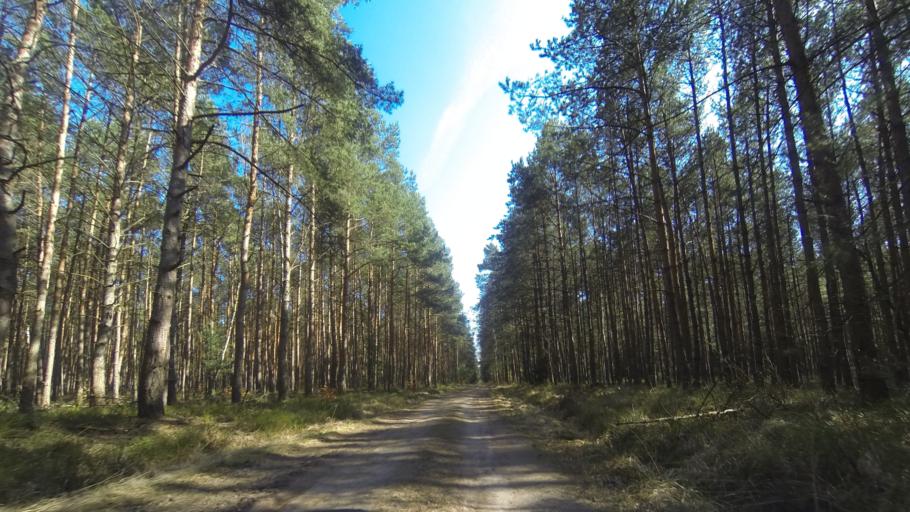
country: DE
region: Saxony
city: Ottendorf-Okrilla
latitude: 51.2161
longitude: 13.7976
